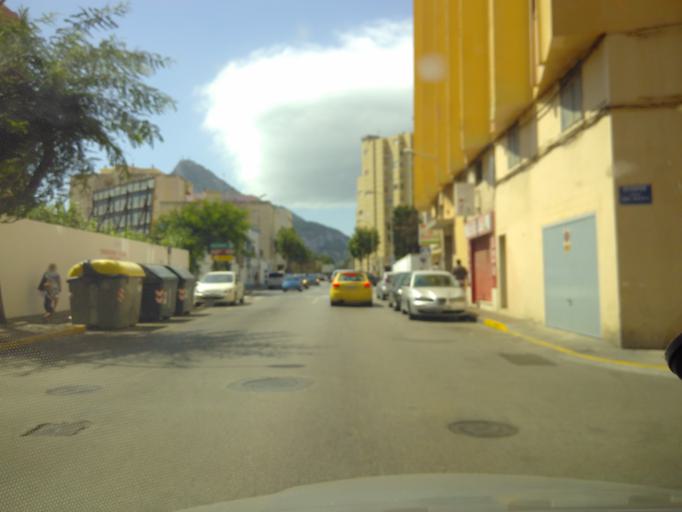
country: ES
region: Andalusia
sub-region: Provincia de Cadiz
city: La Linea de la Concepcion
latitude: 36.1617
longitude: -5.3472
